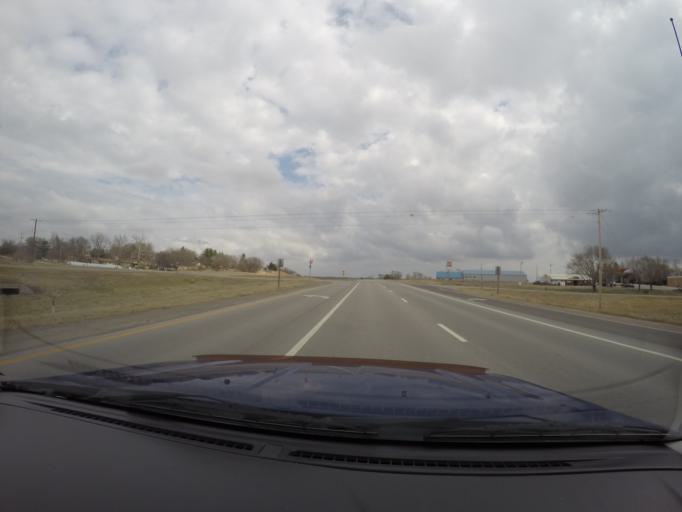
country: US
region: Kansas
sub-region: Riley County
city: Manhattan
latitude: 39.2004
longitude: -96.4407
